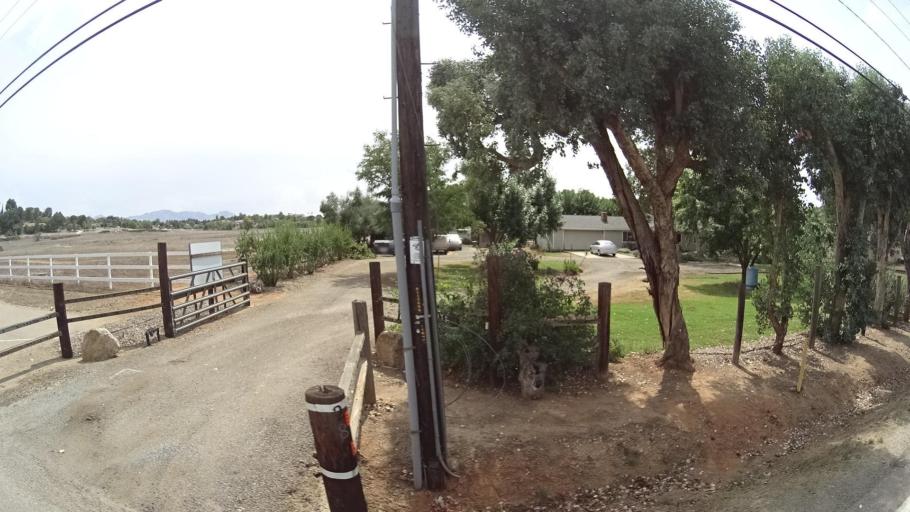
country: US
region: California
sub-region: San Diego County
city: Ramona
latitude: 33.0083
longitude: -116.8981
